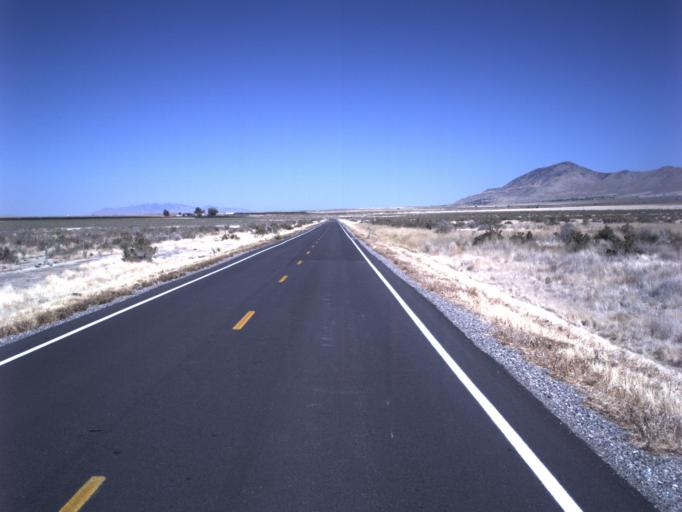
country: US
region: Utah
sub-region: Tooele County
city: Grantsville
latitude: 40.4716
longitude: -112.7463
